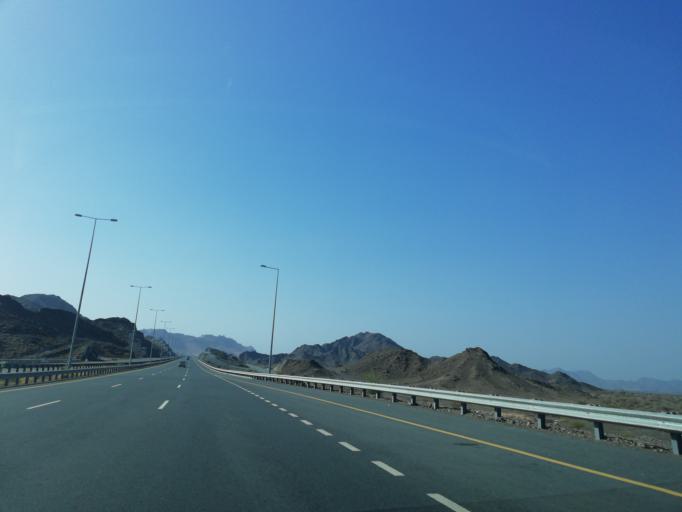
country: OM
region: Muhafazat ad Dakhiliyah
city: Sufalat Sama'il
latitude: 22.9768
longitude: 58.2352
